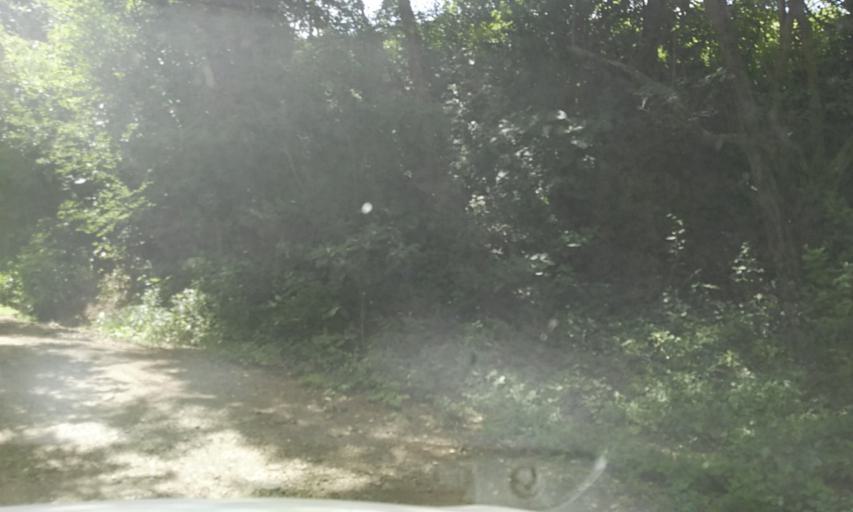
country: NI
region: Matagalpa
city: Terrabona
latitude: 12.6995
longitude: -85.9351
